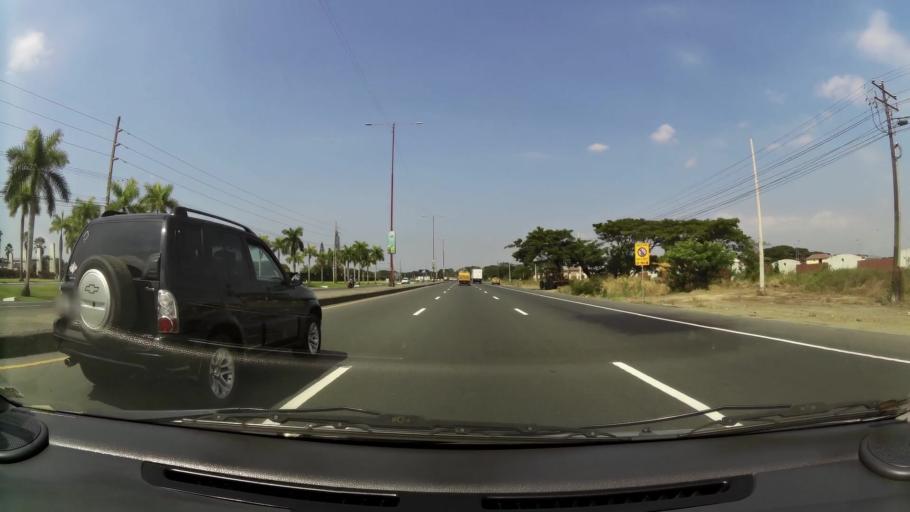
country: EC
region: Guayas
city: Eloy Alfaro
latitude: -2.0511
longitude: -79.9004
